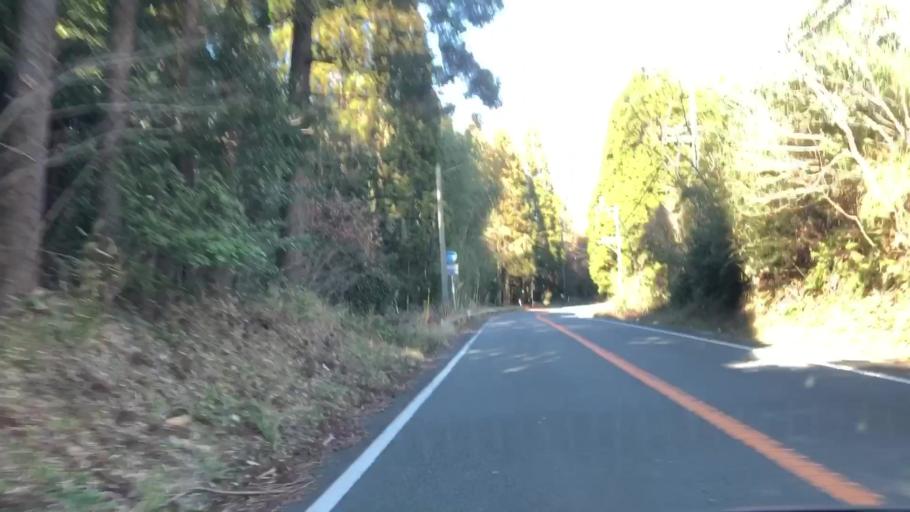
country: JP
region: Kagoshima
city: Satsumasendai
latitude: 31.8558
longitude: 130.4294
